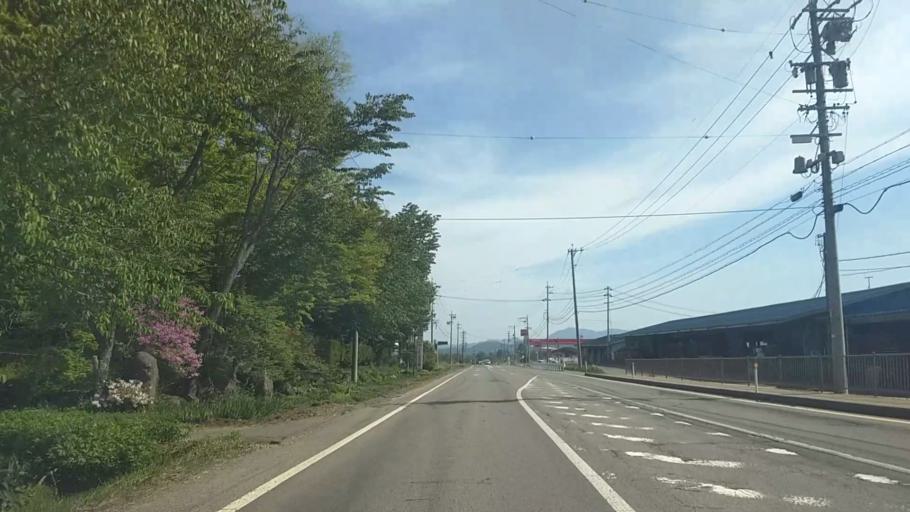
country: JP
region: Nagano
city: Saku
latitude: 35.9823
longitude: 138.4845
